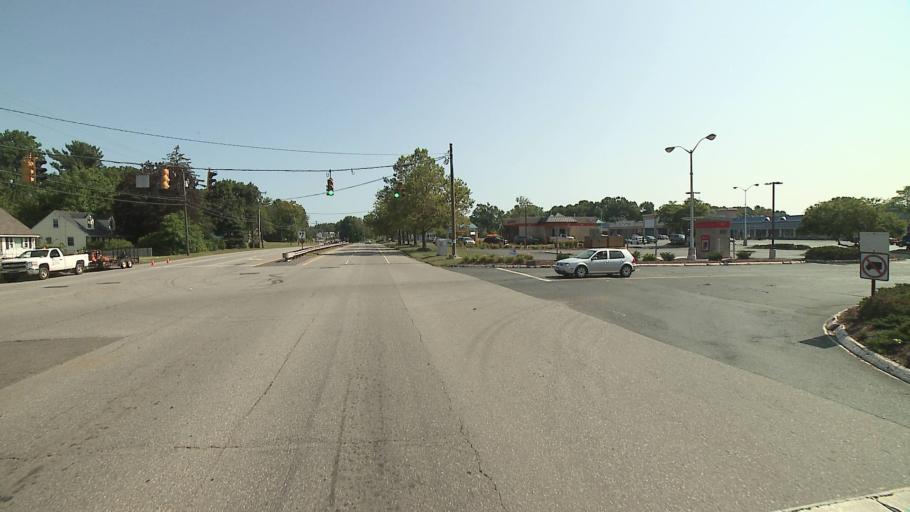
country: US
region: Connecticut
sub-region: Hartford County
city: East Hartford
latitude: 41.7949
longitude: -72.6227
